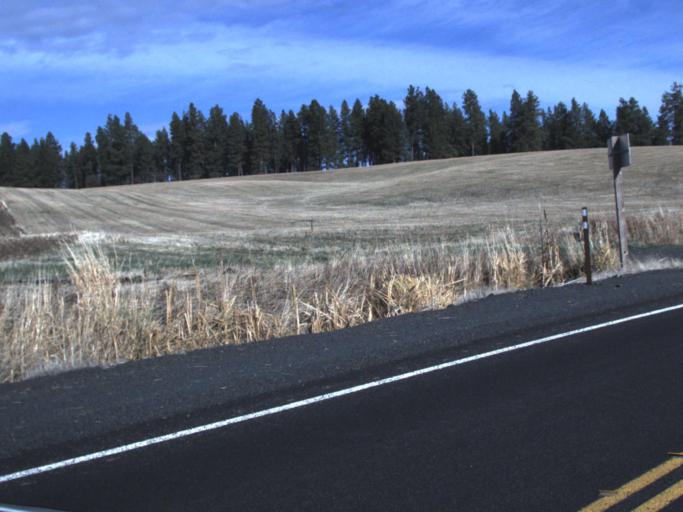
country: US
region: Washington
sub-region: Whitman County
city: Pullman
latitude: 46.9417
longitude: -117.1597
